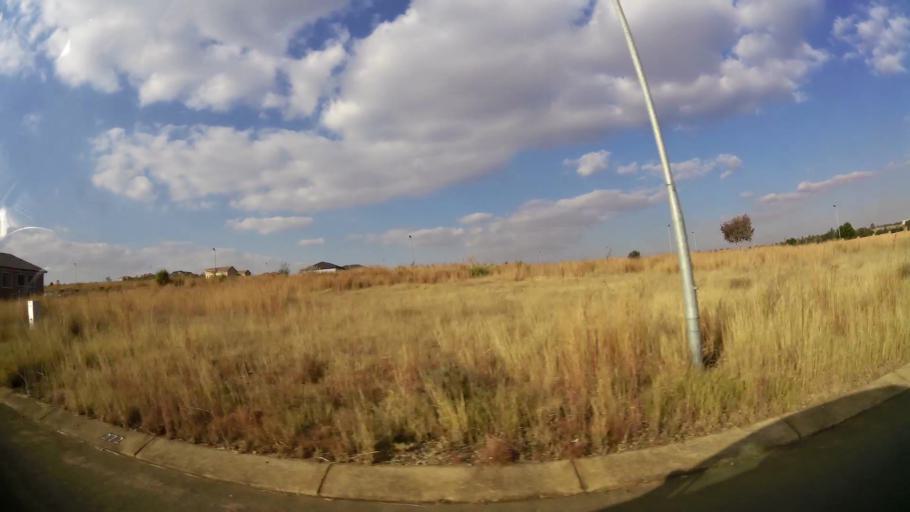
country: ZA
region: Gauteng
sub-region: West Rand District Municipality
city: Krugersdorp
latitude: -26.1043
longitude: 27.7295
